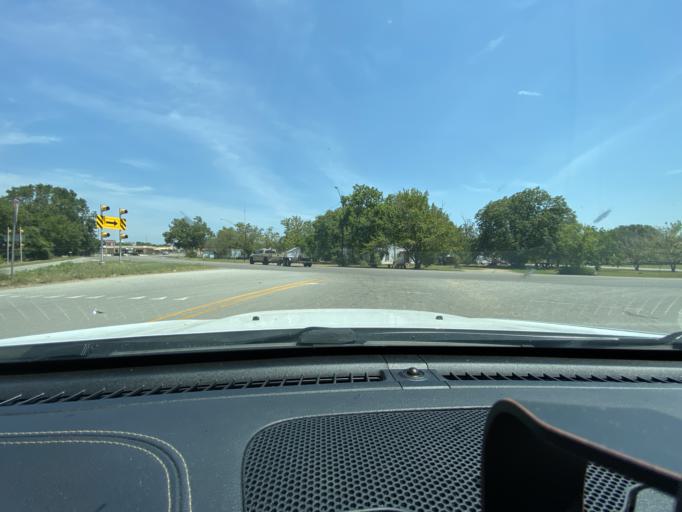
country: US
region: Texas
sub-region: Lee County
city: Giddings
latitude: 30.1771
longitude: -96.9383
